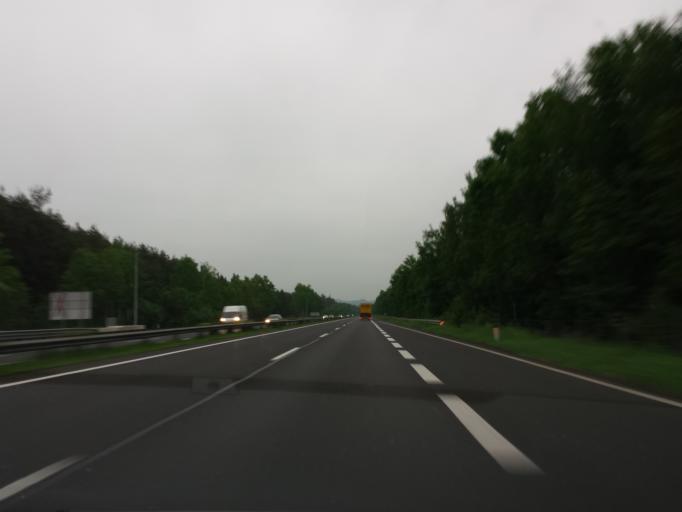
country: AT
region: Styria
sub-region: Politischer Bezirk Hartberg-Fuerstenfeld
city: Hainersdorf
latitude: 47.1149
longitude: 15.9843
